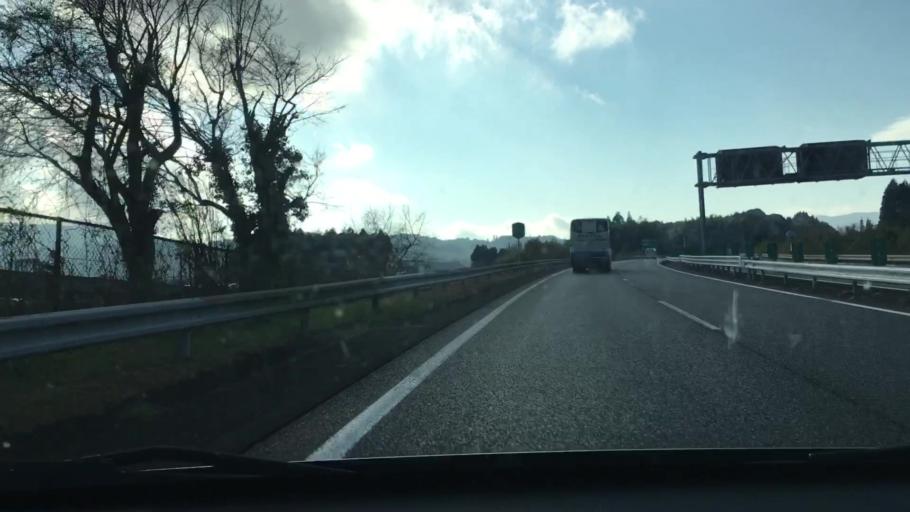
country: JP
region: Kagoshima
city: Okuchi-shinohara
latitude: 32.0250
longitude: 130.7921
